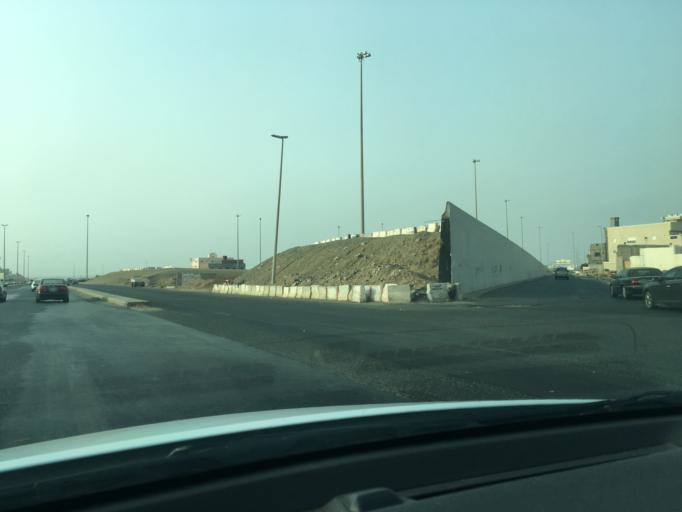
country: SA
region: Makkah
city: Jeddah
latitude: 21.7613
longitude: 39.1836
